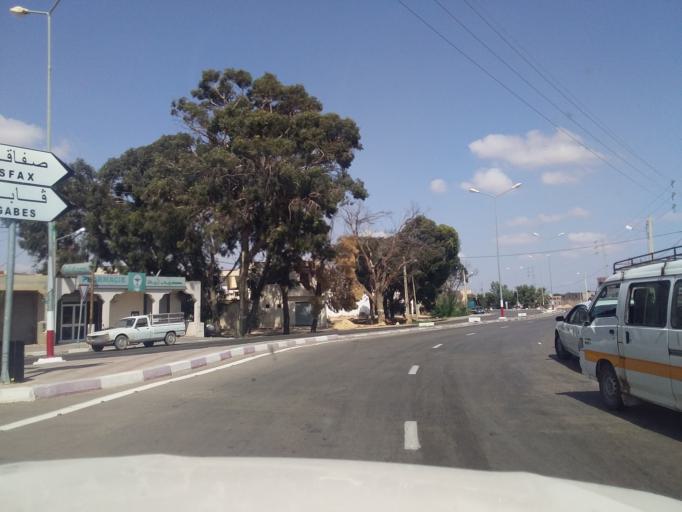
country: TN
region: Madanin
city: Medenine
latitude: 33.5844
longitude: 10.3187
